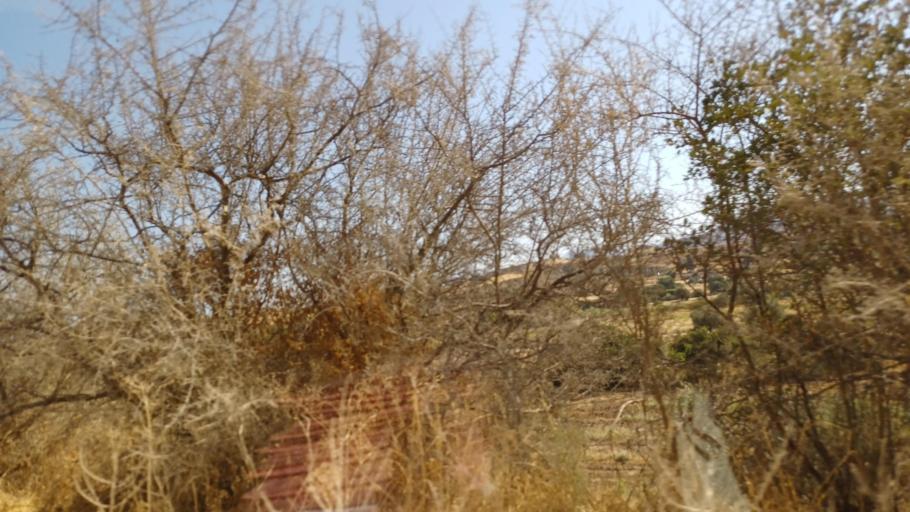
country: CY
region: Pafos
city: Polis
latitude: 35.0086
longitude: 32.4298
